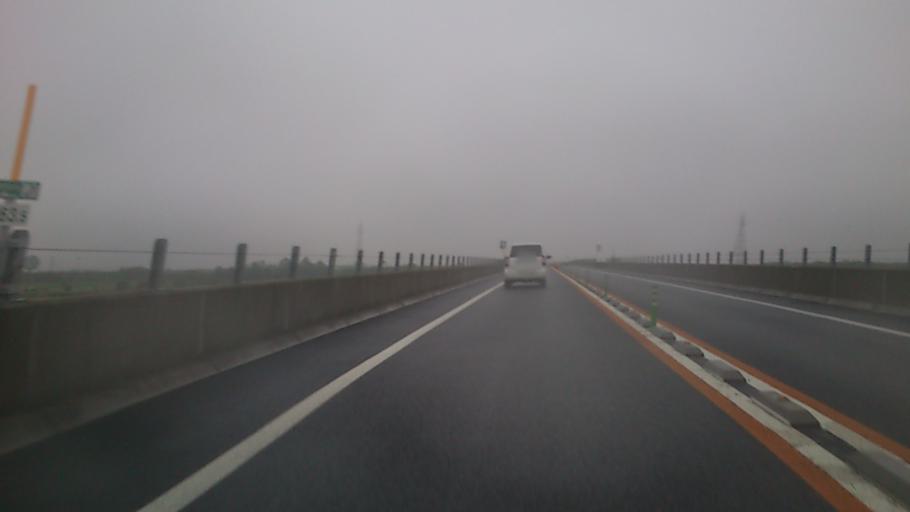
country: JP
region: Hokkaido
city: Kushiro
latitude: 43.0333
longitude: 144.3850
